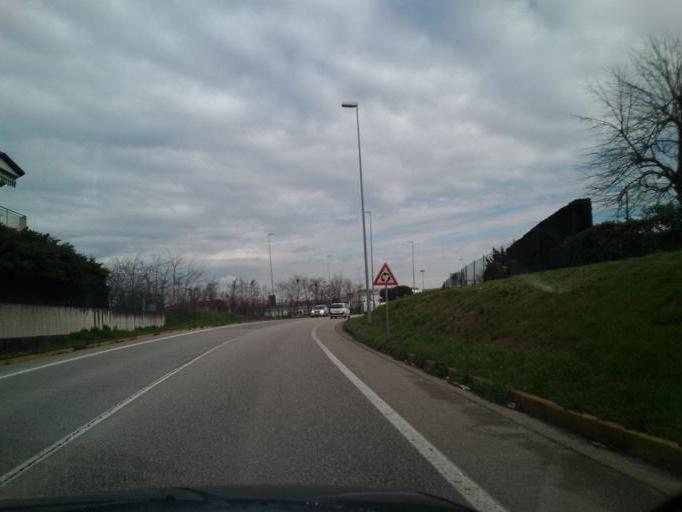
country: IT
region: Veneto
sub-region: Provincia di Verona
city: Villafranca di Verona
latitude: 45.3611
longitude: 10.8419
